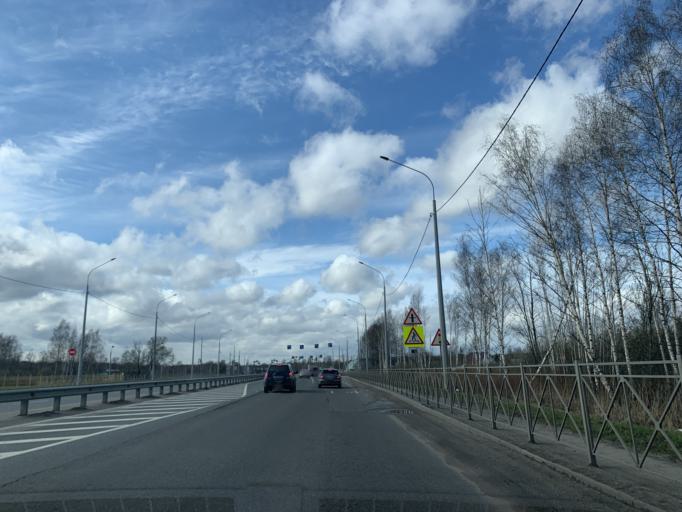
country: RU
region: Jaroslavl
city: Yaroslavl
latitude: 57.6694
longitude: 39.9484
